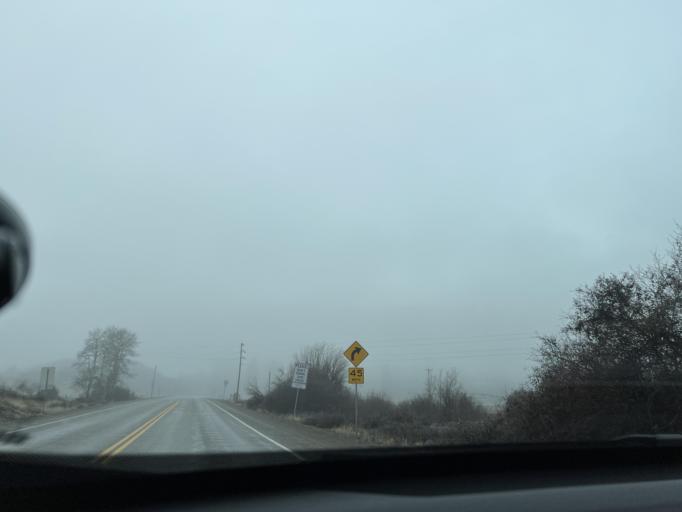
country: US
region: Washington
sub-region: Okanogan County
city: Brewster
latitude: 48.4721
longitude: -120.1968
